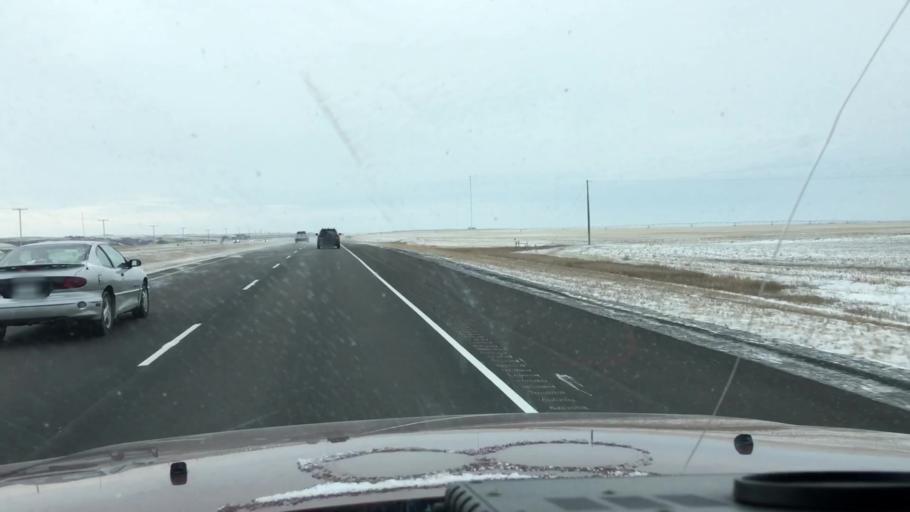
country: CA
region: Saskatchewan
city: Saskatoon
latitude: 51.7518
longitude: -106.4764
